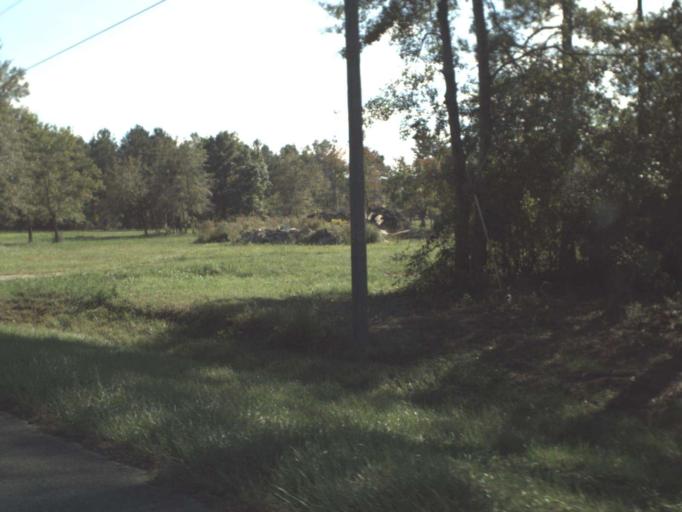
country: US
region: Florida
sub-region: Gulf County
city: Wewahitchka
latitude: 30.0364
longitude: -85.1833
